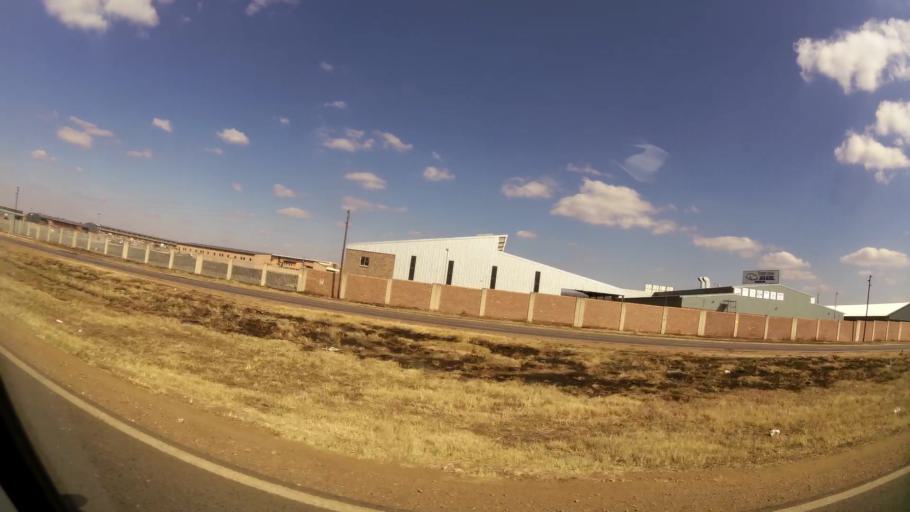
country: ZA
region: Gauteng
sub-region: City of Tshwane Metropolitan Municipality
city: Cullinan
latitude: -25.7500
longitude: 28.3652
